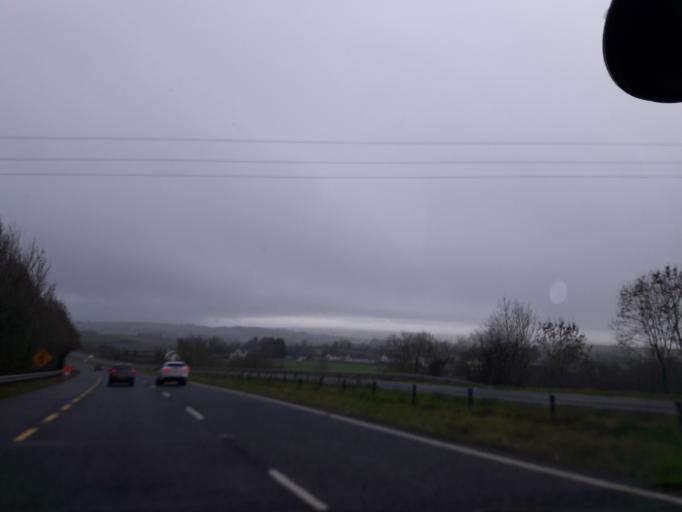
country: IE
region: Ulster
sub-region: County Donegal
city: Letterkenny
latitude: 54.9478
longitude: -7.6494
